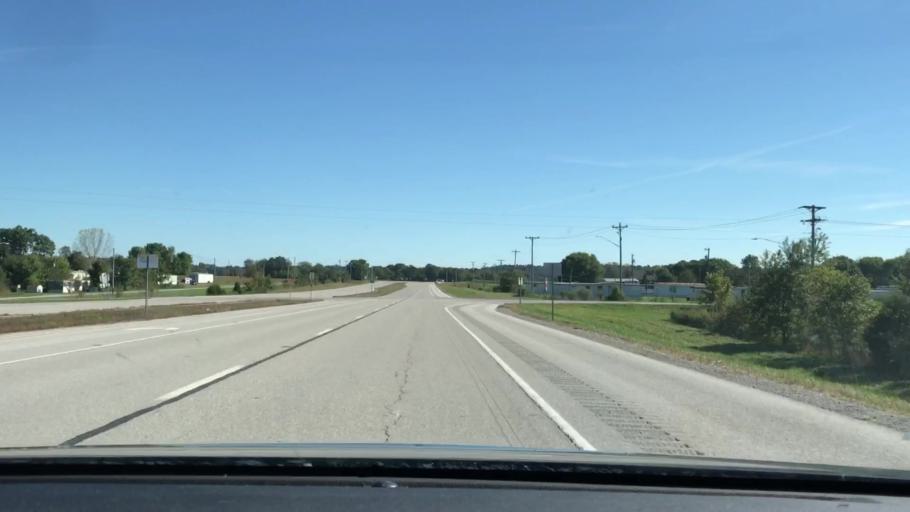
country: US
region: Kentucky
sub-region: Todd County
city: Elkton
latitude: 36.8226
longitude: -87.1662
